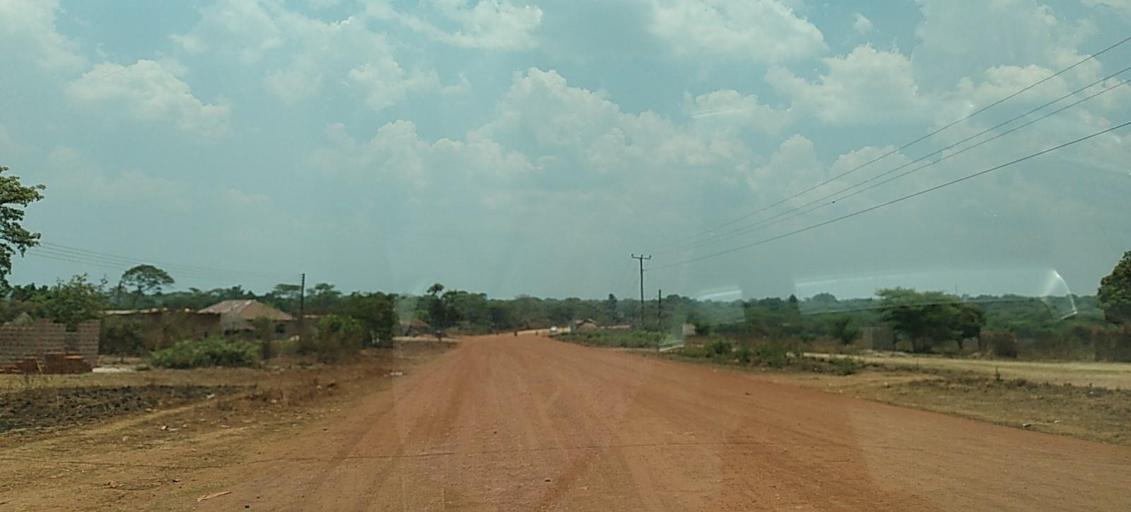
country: ZM
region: Copperbelt
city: Chingola
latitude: -12.8702
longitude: 27.5992
